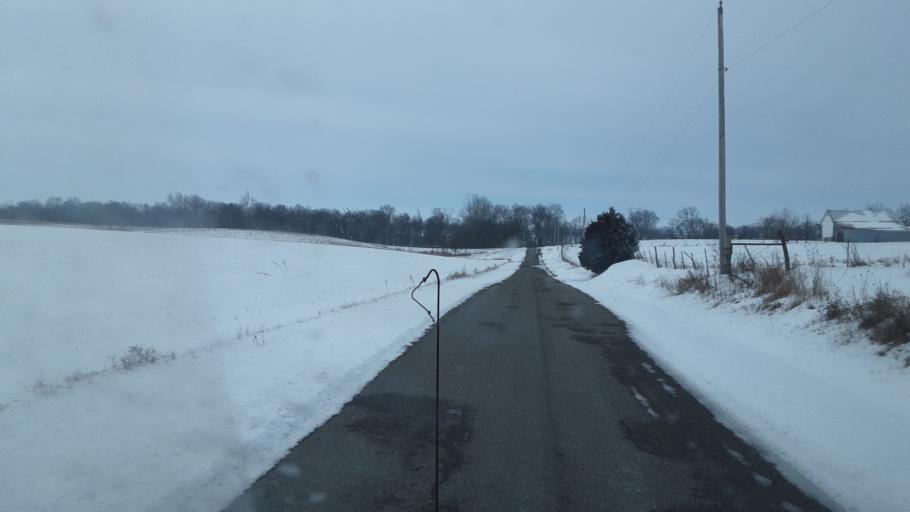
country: US
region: Ohio
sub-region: Union County
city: Marysville
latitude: 40.1733
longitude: -83.4053
